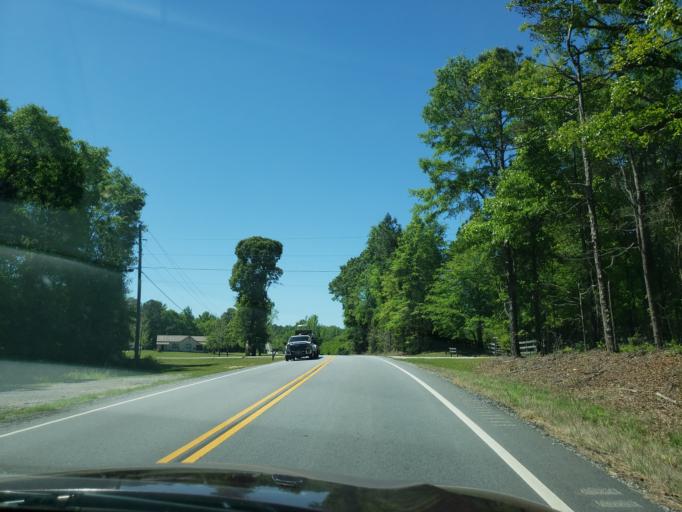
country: US
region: Alabama
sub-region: Tallapoosa County
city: Dadeville
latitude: 32.6831
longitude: -85.7873
